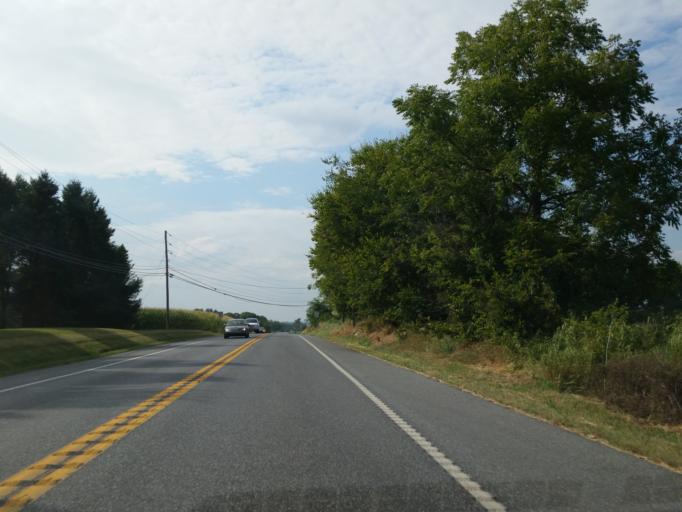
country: US
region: Pennsylvania
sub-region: Lebanon County
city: Annville
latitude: 40.3033
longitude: -76.4958
